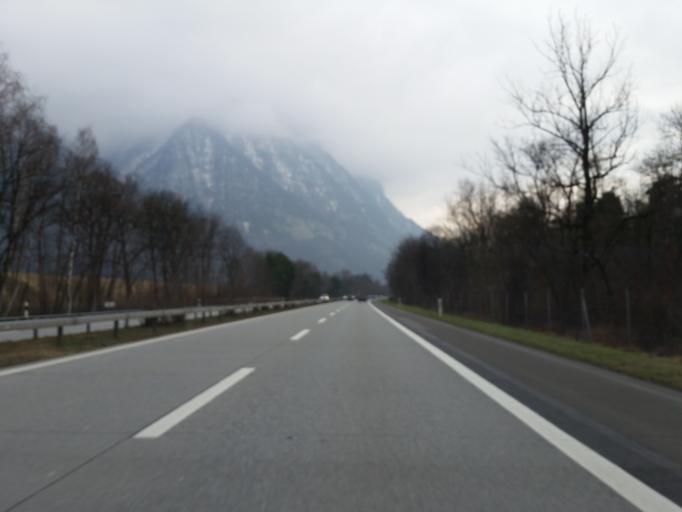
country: LI
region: Triesen
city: Triesen
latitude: 47.1061
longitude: 9.5171
